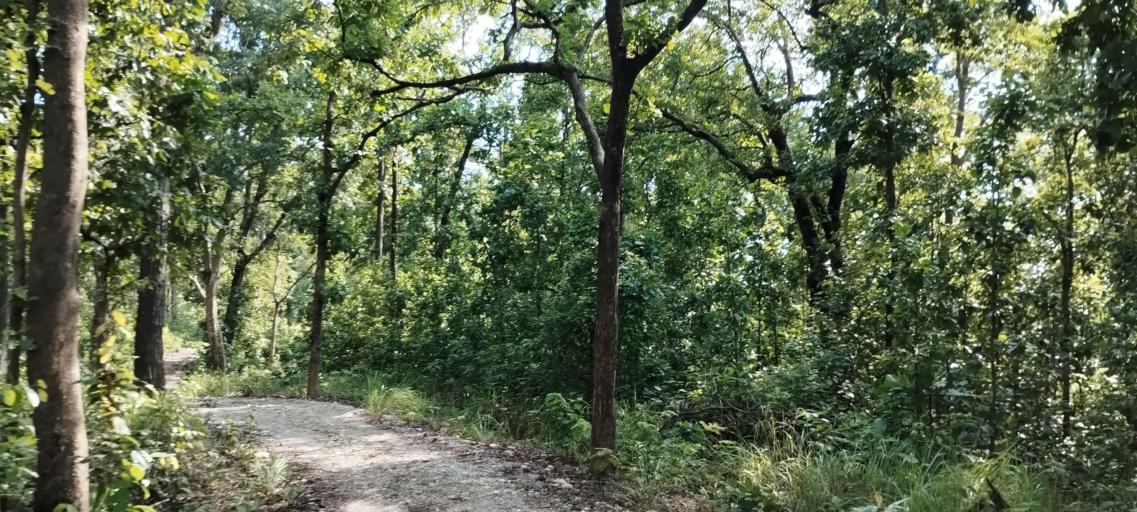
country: NP
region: Far Western
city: Tikapur
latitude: 28.5613
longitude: 81.2662
